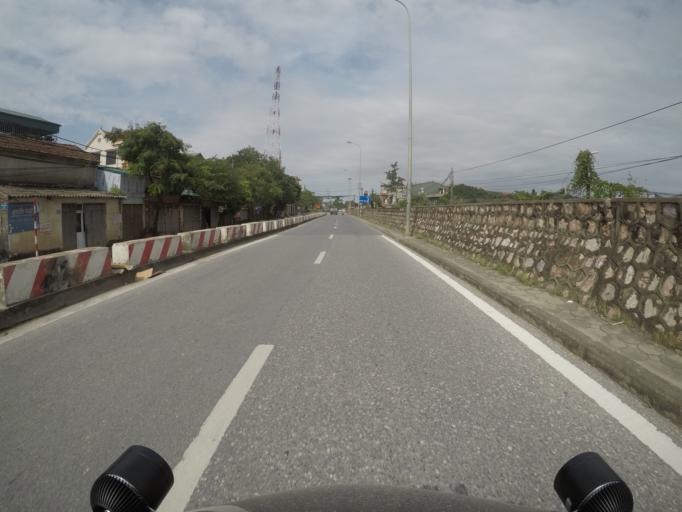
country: VN
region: Ha Noi
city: Tay Ho
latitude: 21.0935
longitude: 105.7790
